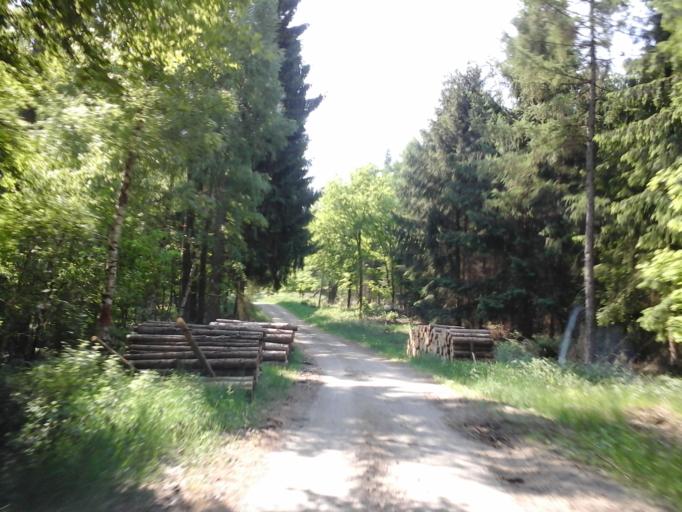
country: PL
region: West Pomeranian Voivodeship
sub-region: Powiat choszczenski
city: Recz
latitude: 53.3115
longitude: 15.6022
